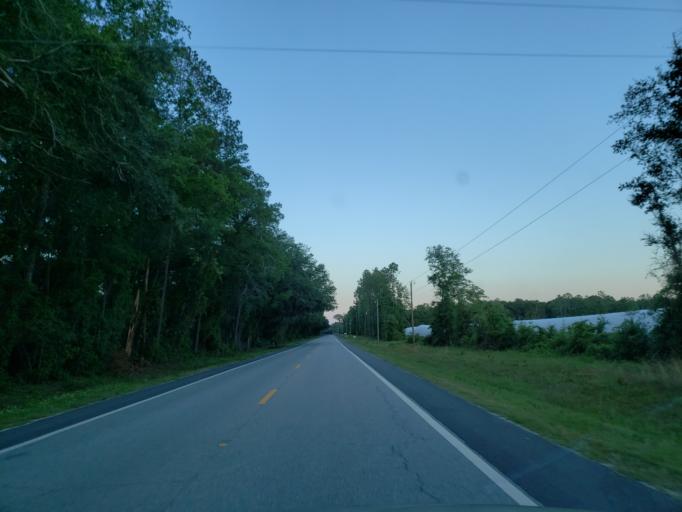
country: US
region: Georgia
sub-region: Echols County
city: Statenville
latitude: 30.5554
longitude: -83.1180
